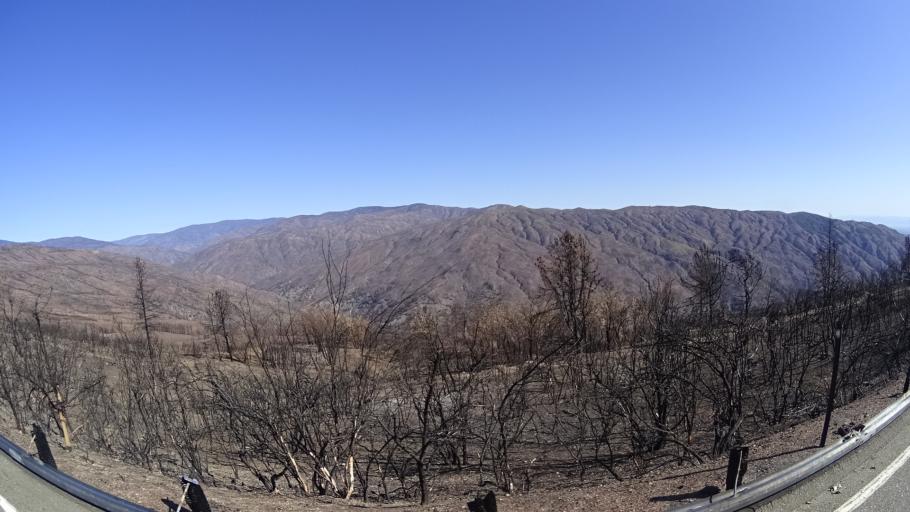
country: US
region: California
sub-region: Tehama County
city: Rancho Tehama Reserve
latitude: 39.6674
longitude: -122.6726
